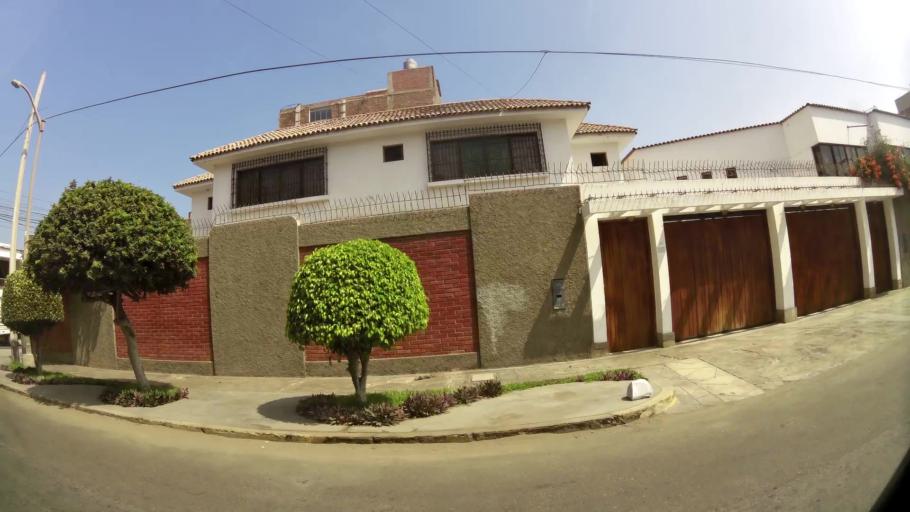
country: PE
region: La Libertad
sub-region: Provincia de Trujillo
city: Buenos Aires
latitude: -8.1286
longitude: -79.0378
